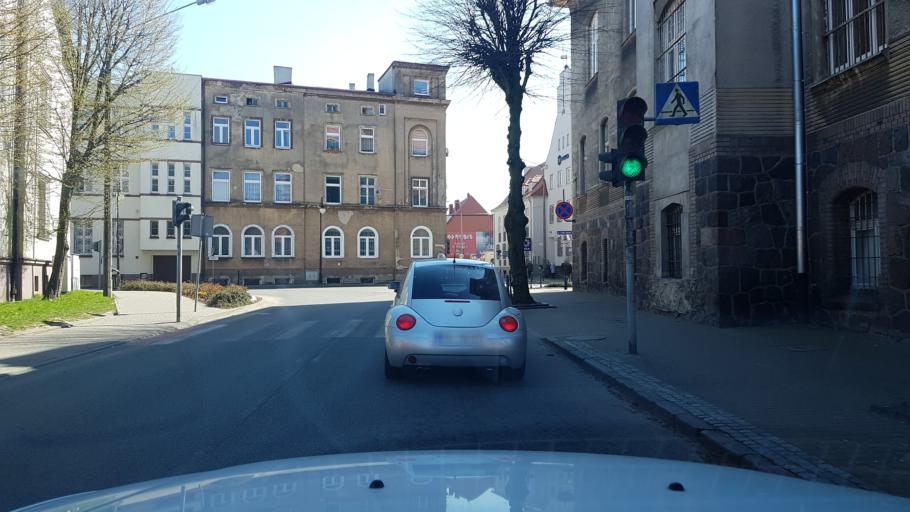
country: PL
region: West Pomeranian Voivodeship
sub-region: Powiat slawienski
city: Slawno
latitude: 54.3654
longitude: 16.6788
